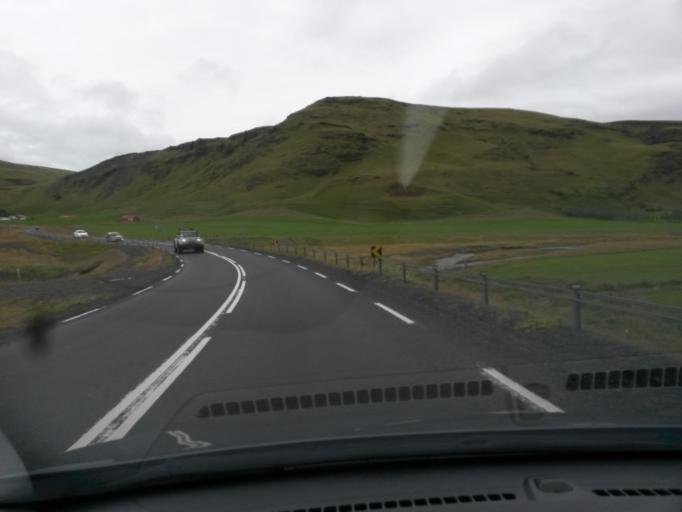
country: IS
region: South
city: Vestmannaeyjar
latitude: 63.4546
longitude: -19.0640
